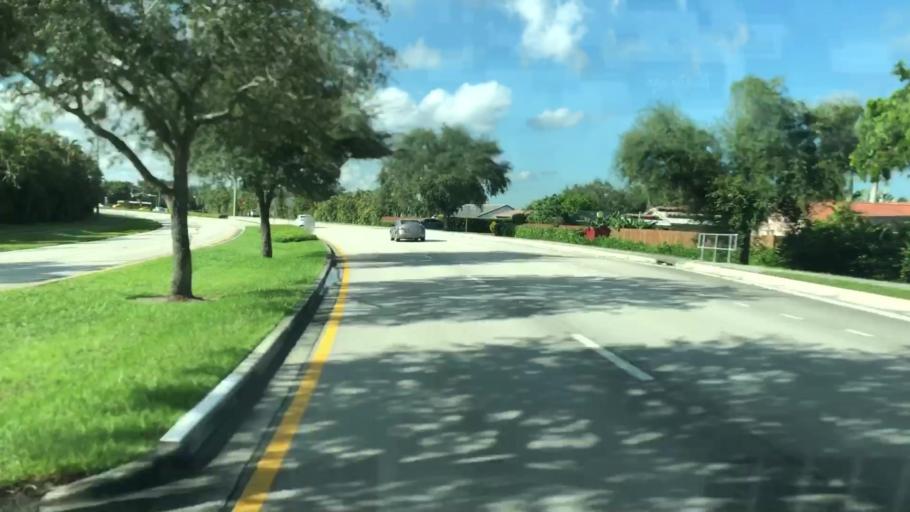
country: US
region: Florida
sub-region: Broward County
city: Tamarac
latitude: 26.2355
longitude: -80.2706
